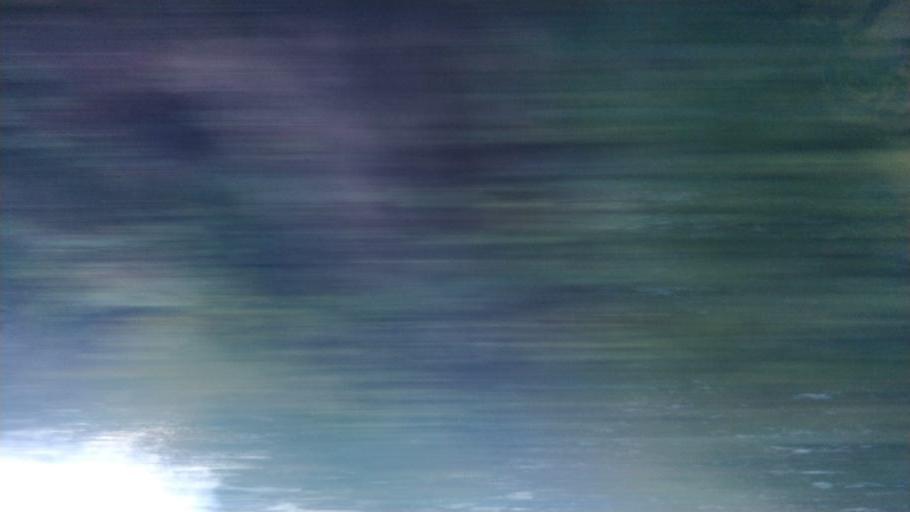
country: GB
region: England
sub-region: Lancashire
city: Appley Bridge
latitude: 53.5807
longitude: -2.7275
